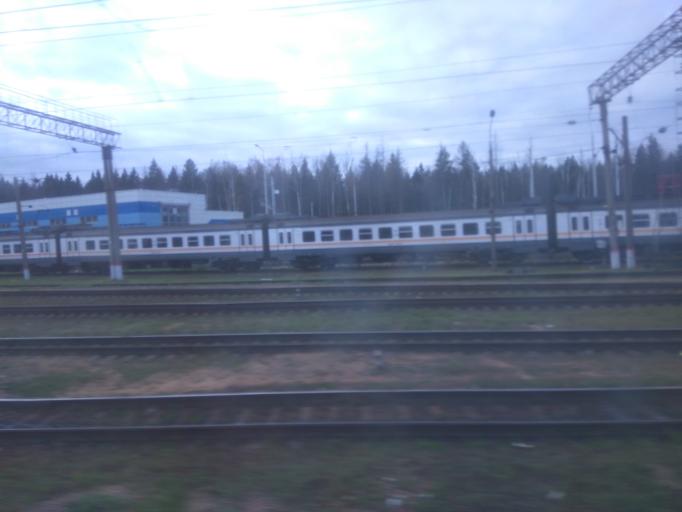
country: RU
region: Moskovskaya
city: Aprelevka
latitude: 55.5619
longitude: 37.0902
